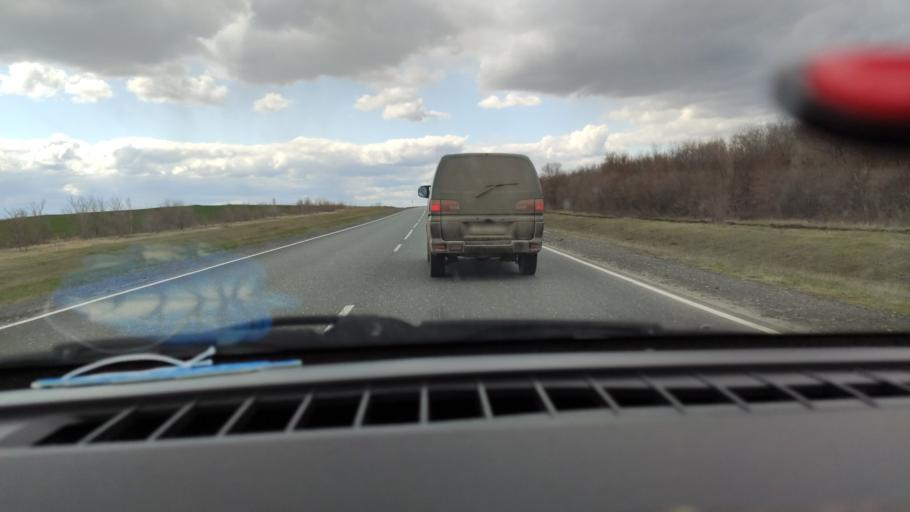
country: RU
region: Saratov
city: Balakovo
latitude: 52.1908
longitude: 47.8528
